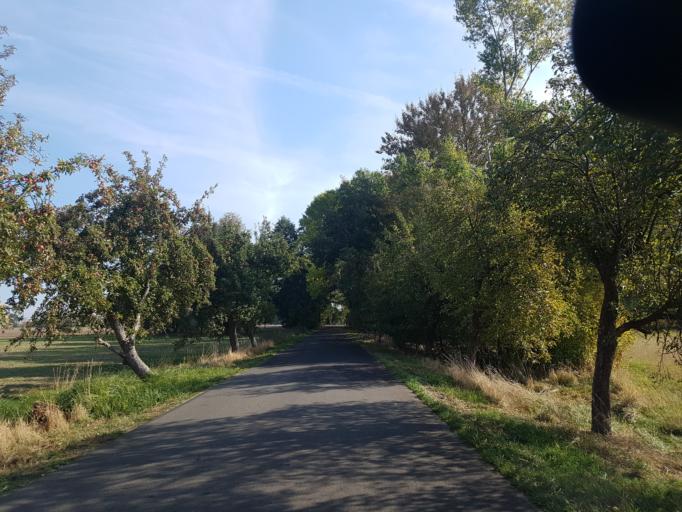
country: DE
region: Brandenburg
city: Ihlow
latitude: 51.8341
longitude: 13.3390
